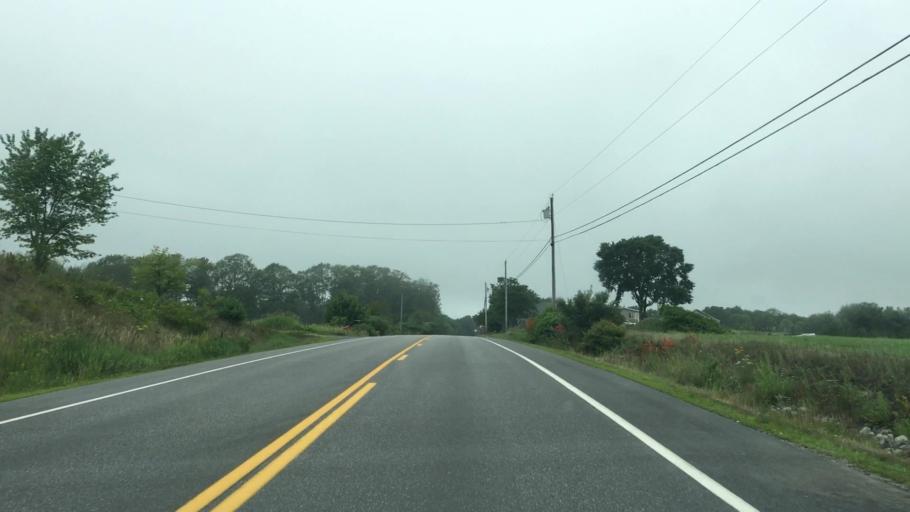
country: US
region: Maine
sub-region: Sagadahoc County
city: Richmond
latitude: 44.0895
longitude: -69.7082
